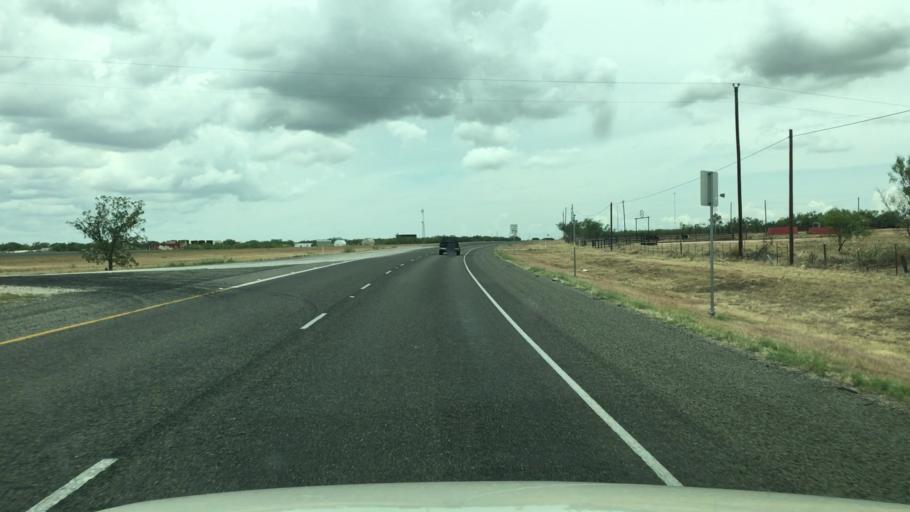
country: US
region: Texas
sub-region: Concho County
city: Eden
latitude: 31.2184
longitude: -99.9636
